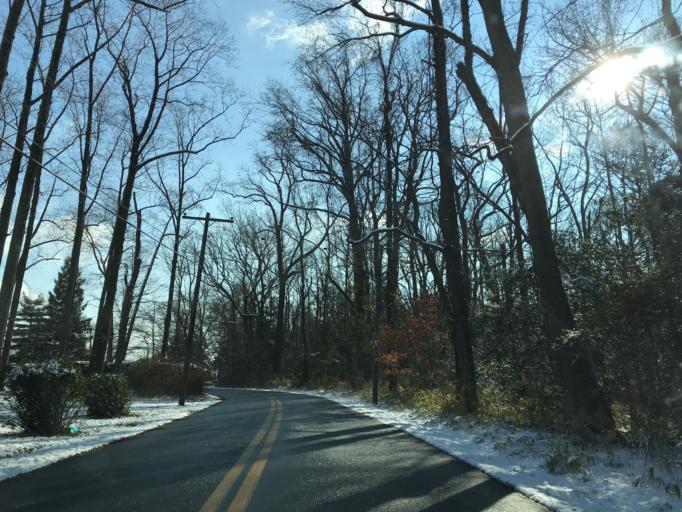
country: US
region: Maryland
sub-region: Baltimore County
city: Bowleys Quarters
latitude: 39.3090
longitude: -76.3727
